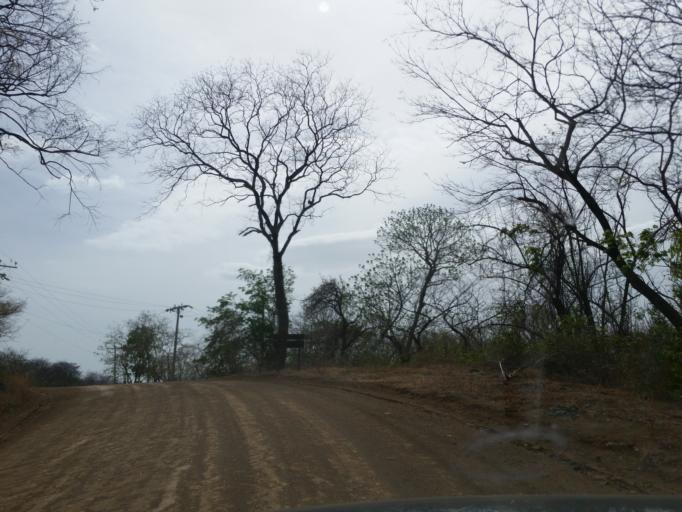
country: NI
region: Rivas
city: Tola
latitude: 11.4451
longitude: -86.0758
